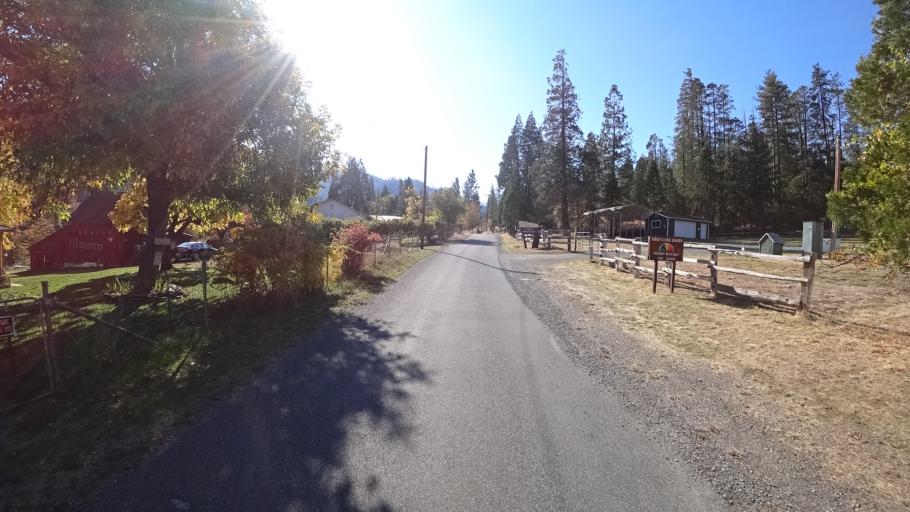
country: US
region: California
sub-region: Siskiyou County
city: Yreka
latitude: 41.7412
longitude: -123.0042
